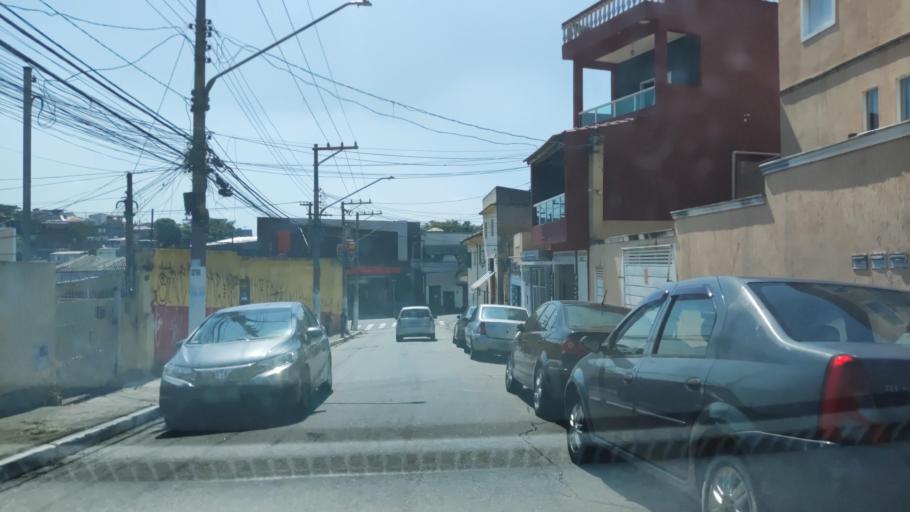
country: BR
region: Sao Paulo
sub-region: Sao Paulo
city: Sao Paulo
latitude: -23.4918
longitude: -46.6629
